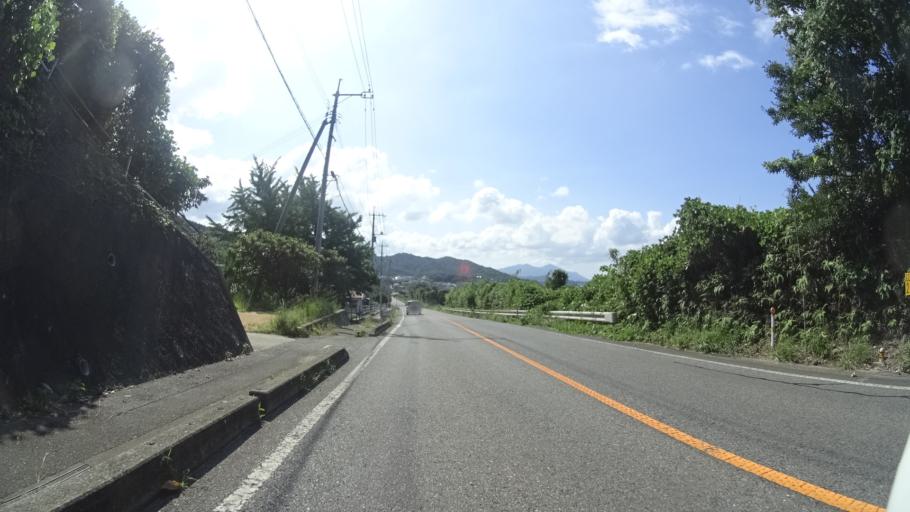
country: JP
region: Yamaguchi
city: Shimonoseki
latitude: 34.2148
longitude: 130.9306
